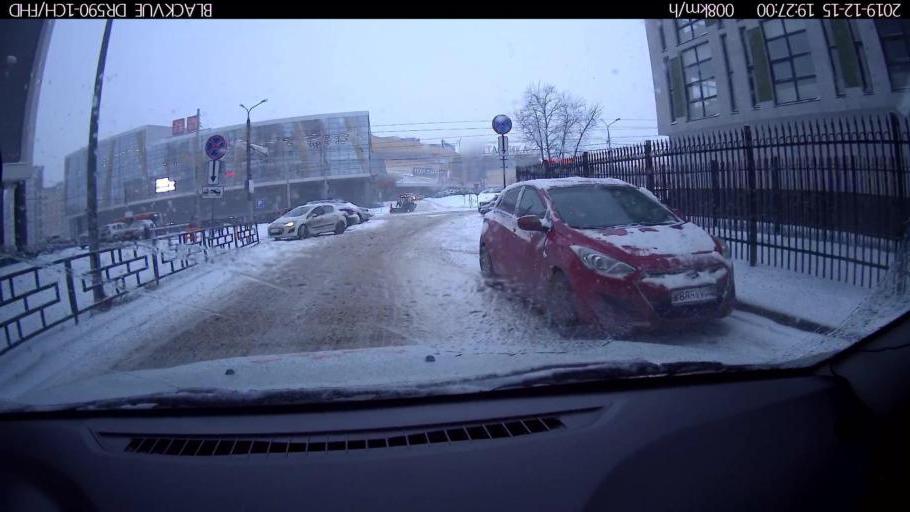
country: RU
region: Nizjnij Novgorod
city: Afonino
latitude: 56.3077
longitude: 44.0797
